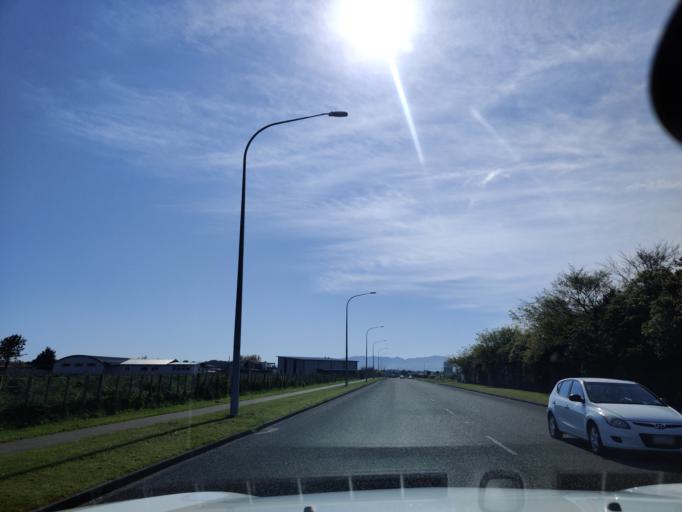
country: NZ
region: Manawatu-Wanganui
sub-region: Palmerston North City
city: Palmerston North
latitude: -40.3331
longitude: 175.6469
